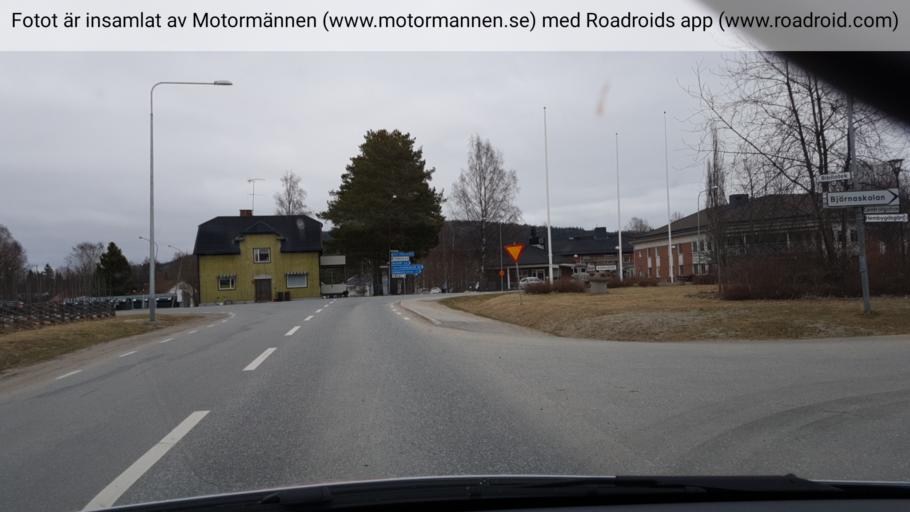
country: SE
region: Vaesternorrland
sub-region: OErnskoeldsviks Kommun
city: Ornskoldsvik
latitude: 63.5502
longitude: 18.5984
